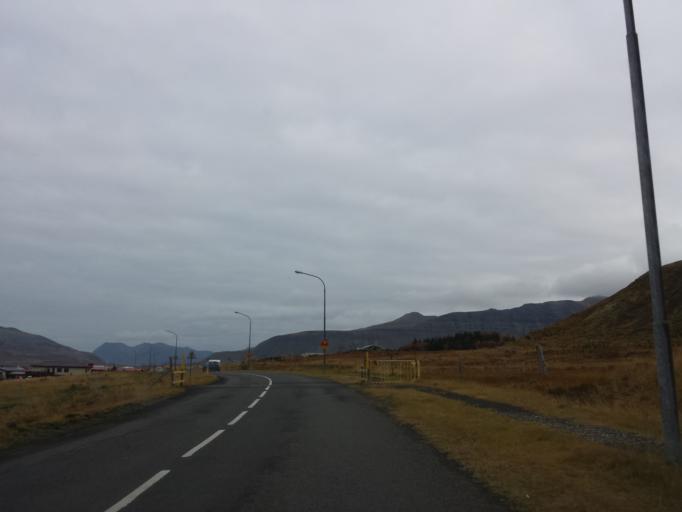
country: IS
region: West
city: Olafsvik
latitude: 64.9222
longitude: -23.2788
